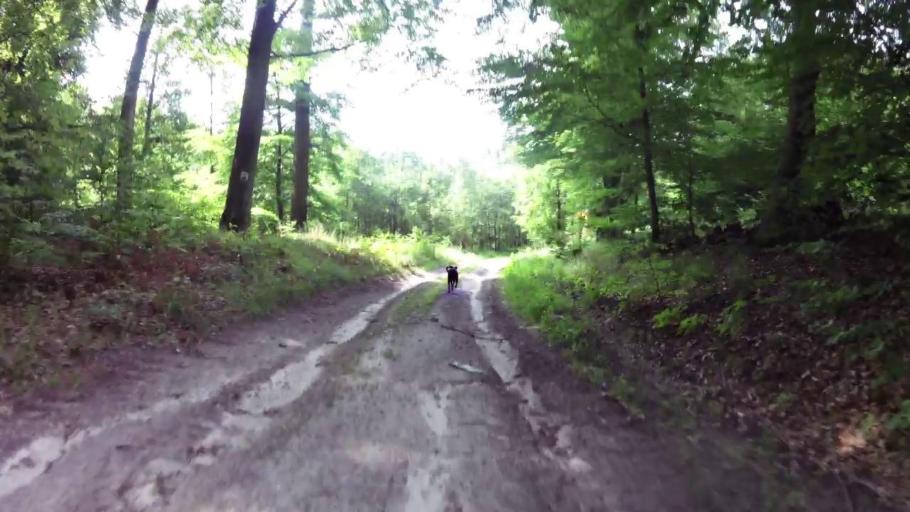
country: PL
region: West Pomeranian Voivodeship
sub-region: Powiat lobeski
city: Wegorzyno
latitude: 53.5138
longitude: 15.6792
